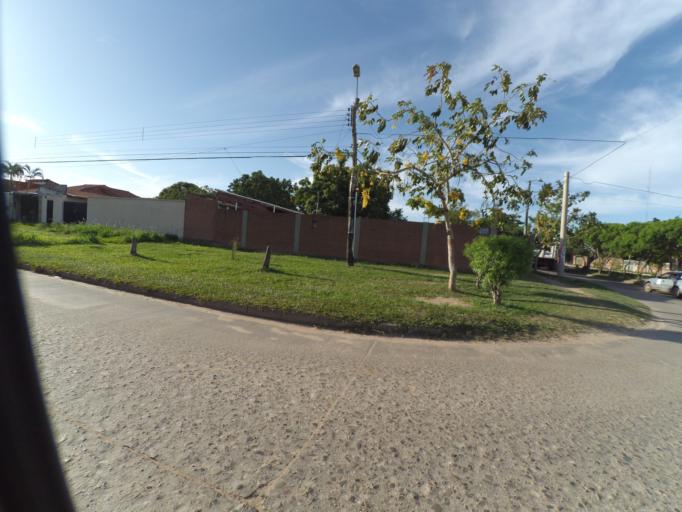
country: BO
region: Santa Cruz
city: Santa Cruz de la Sierra
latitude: -17.7770
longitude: -63.1323
